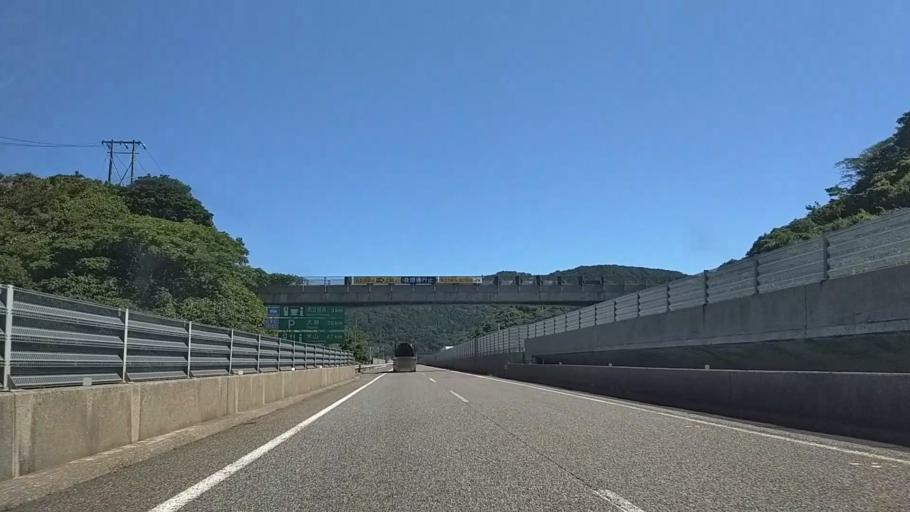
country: JP
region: Niigata
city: Joetsu
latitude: 37.1538
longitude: 138.0803
